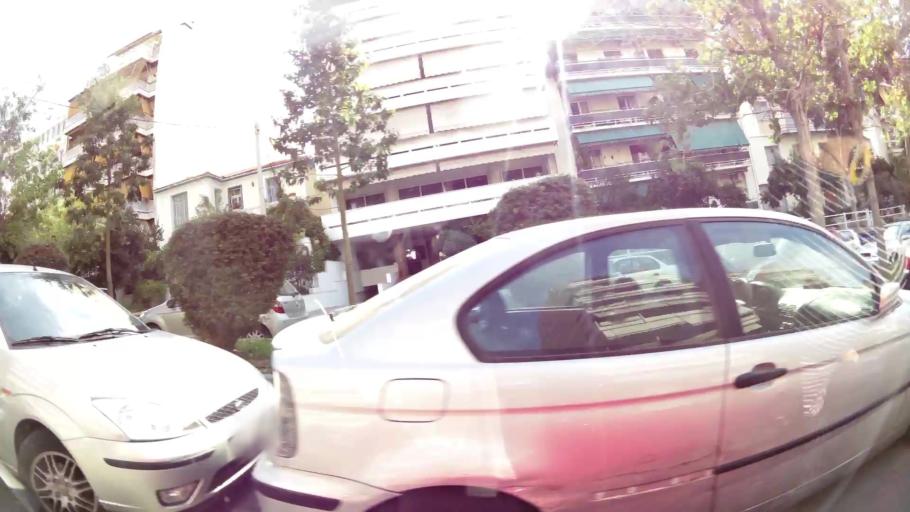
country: GR
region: Attica
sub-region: Nomarchia Athinas
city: Kallithea
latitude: 37.9462
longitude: 23.7050
